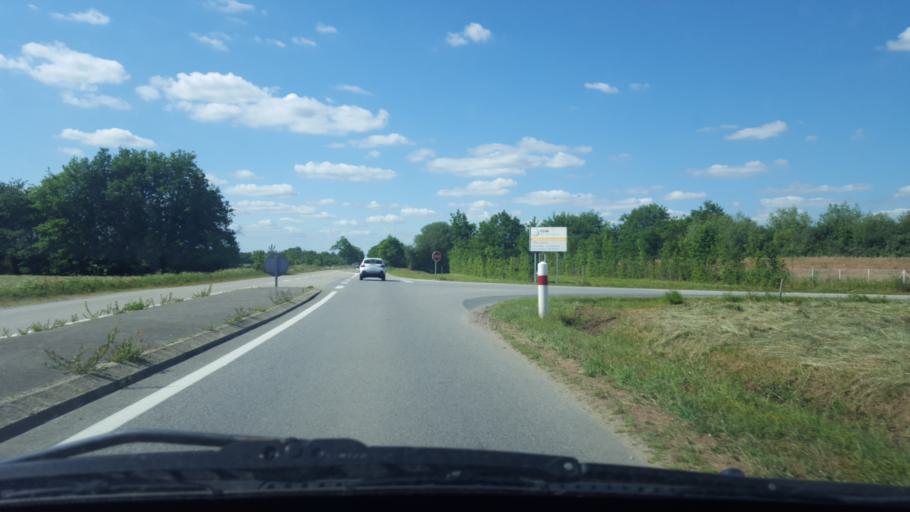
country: FR
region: Pays de la Loire
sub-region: Departement de la Loire-Atlantique
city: Geneston
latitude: 47.0506
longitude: -1.5662
